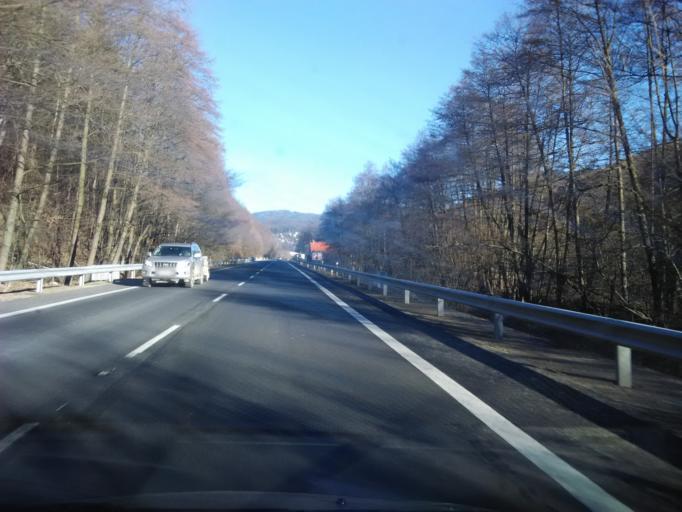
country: SK
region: Banskobystricky
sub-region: Okres Ziar nad Hronom
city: Kremnica
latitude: 48.6404
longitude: 18.9020
